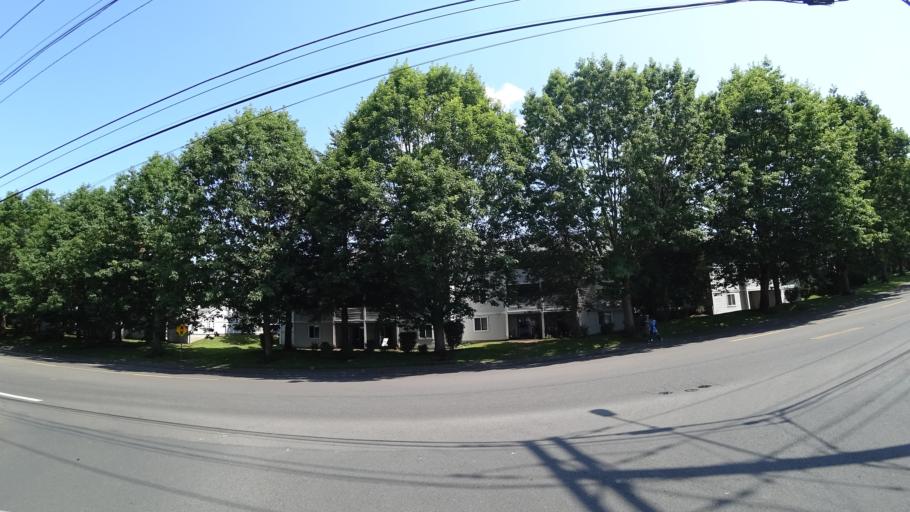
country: US
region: Oregon
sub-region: Clackamas County
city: Oatfield
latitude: 45.4471
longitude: -122.5913
